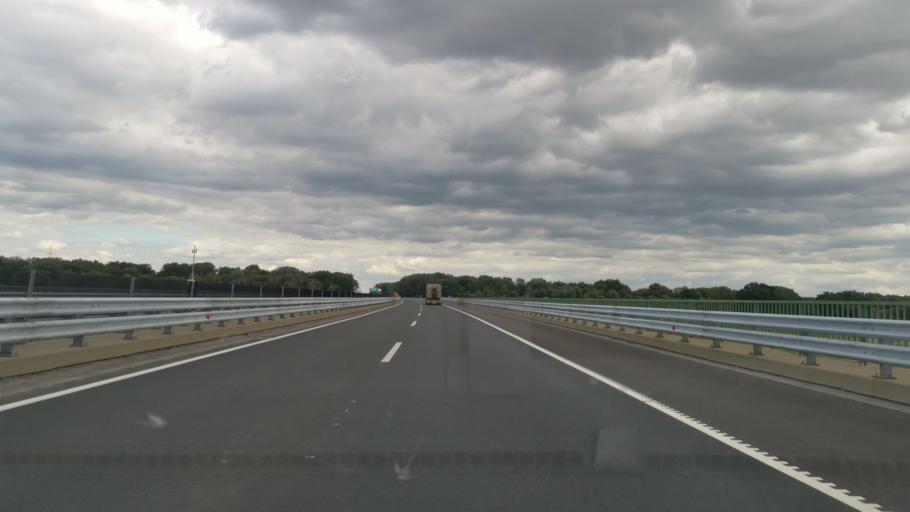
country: HU
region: Jasz-Nagykun-Szolnok
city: Szajol
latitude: 47.2107
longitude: 20.2818
